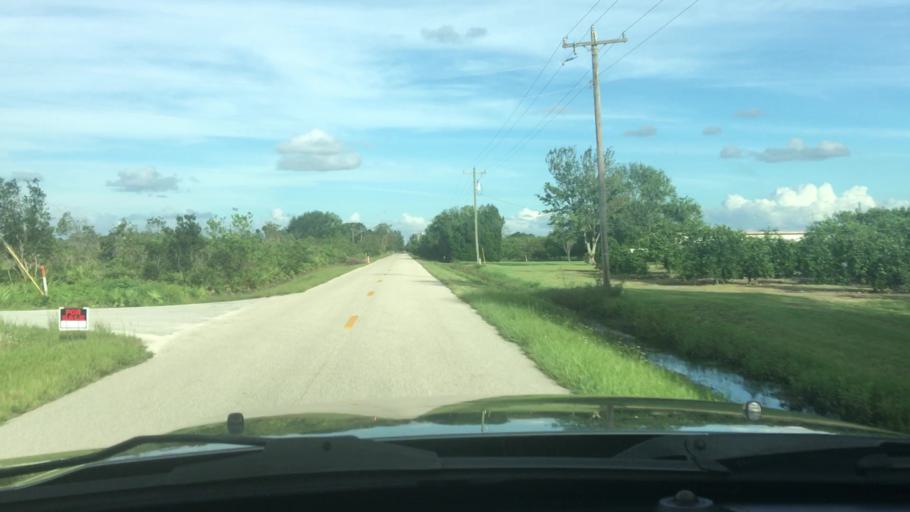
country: US
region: Florida
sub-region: Highlands County
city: Sebring
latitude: 27.4630
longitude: -81.2441
